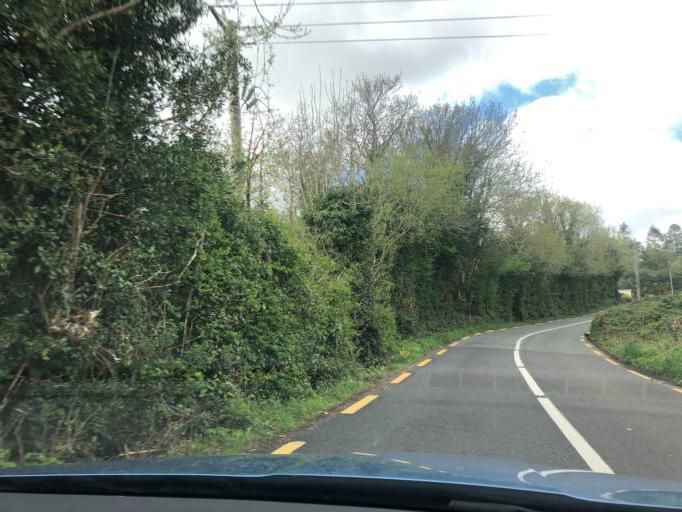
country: IE
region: Munster
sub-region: Ciarrai
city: Killorglin
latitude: 51.8202
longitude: -9.8762
